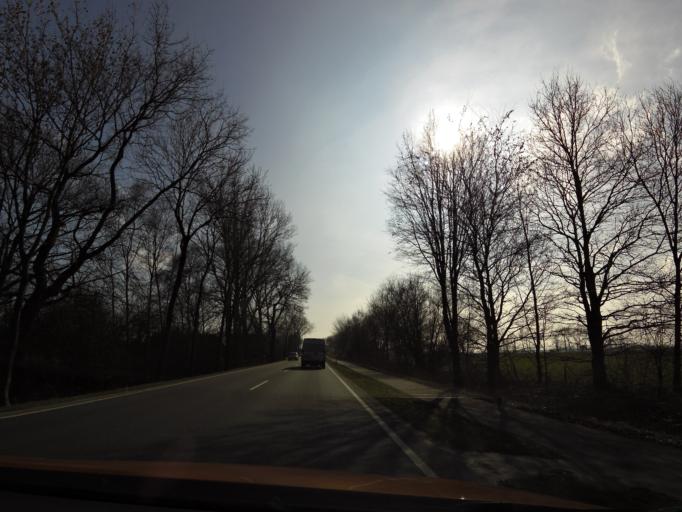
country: DE
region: Lower Saxony
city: Elsfleth
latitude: 53.2152
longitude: 8.4452
